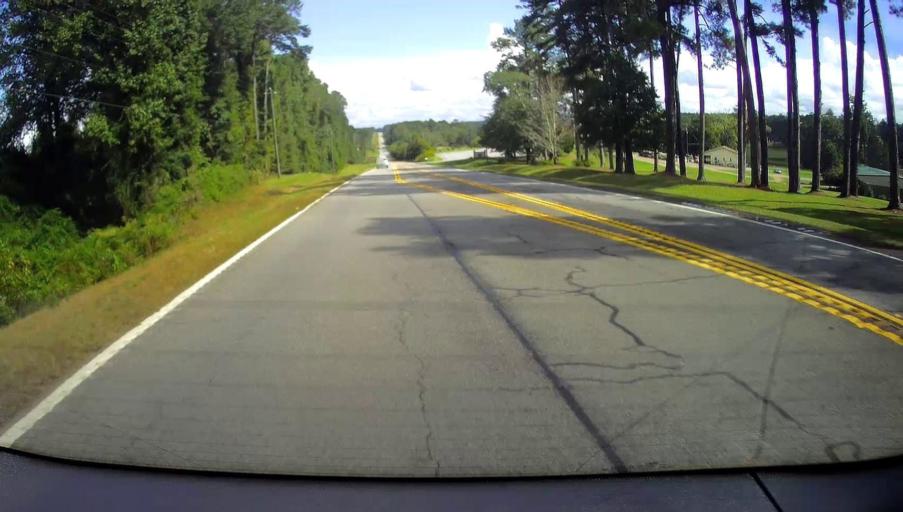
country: US
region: Georgia
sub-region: Jones County
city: Gray
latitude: 33.0271
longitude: -83.4763
